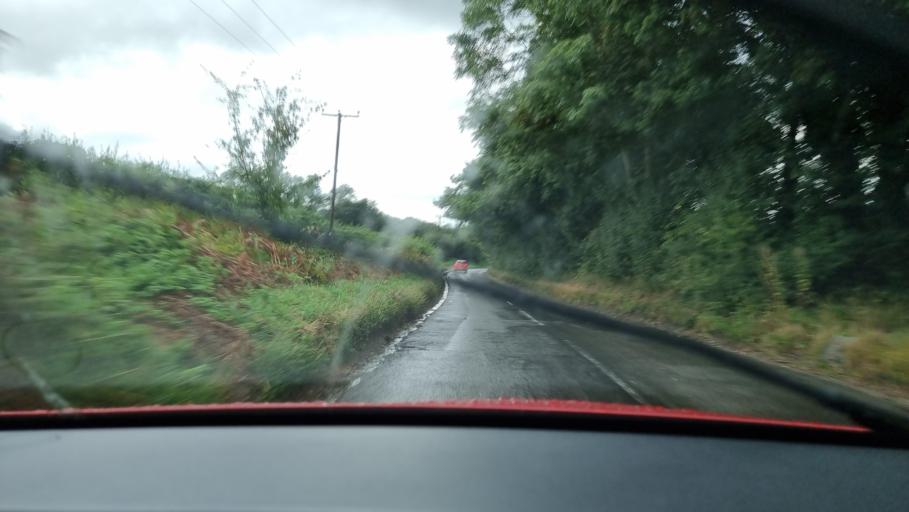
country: GB
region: England
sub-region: Buckinghamshire
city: Chesham
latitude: 51.7252
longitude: -0.5809
